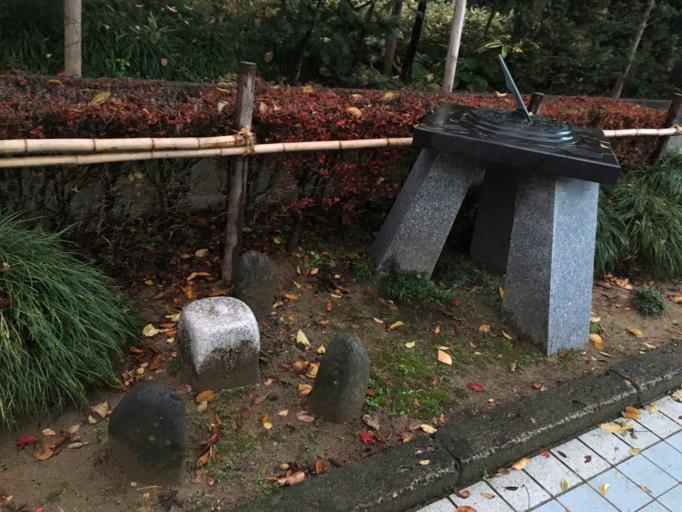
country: JP
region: Toyama
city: Toyama-shi
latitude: 36.6951
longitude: 137.2135
